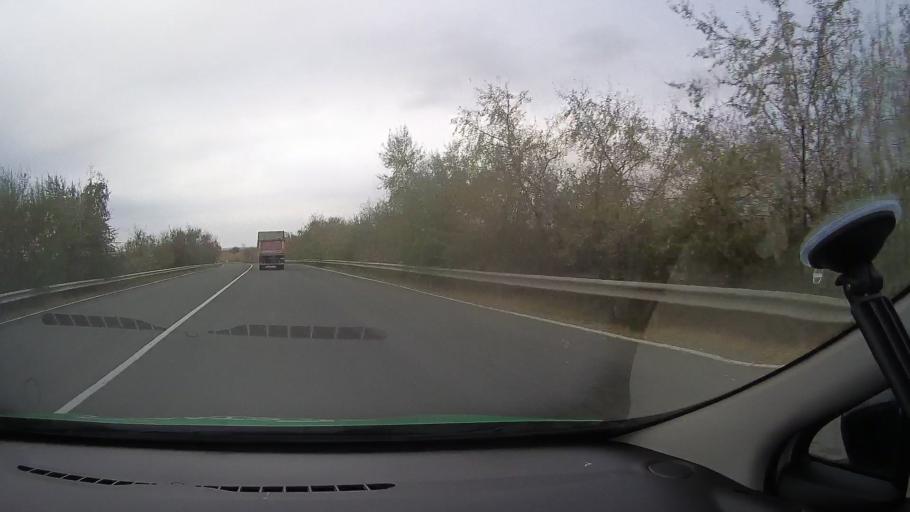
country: RO
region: Constanta
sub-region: Comuna Poarta Alba
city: Poarta Alba
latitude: 44.2187
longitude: 28.3887
